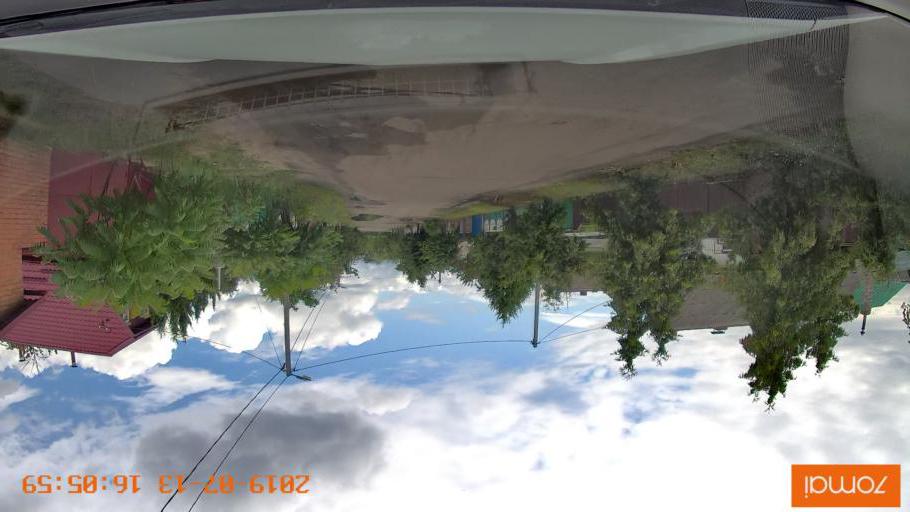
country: BY
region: Mogilev
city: Babruysk
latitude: 53.1513
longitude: 29.2049
